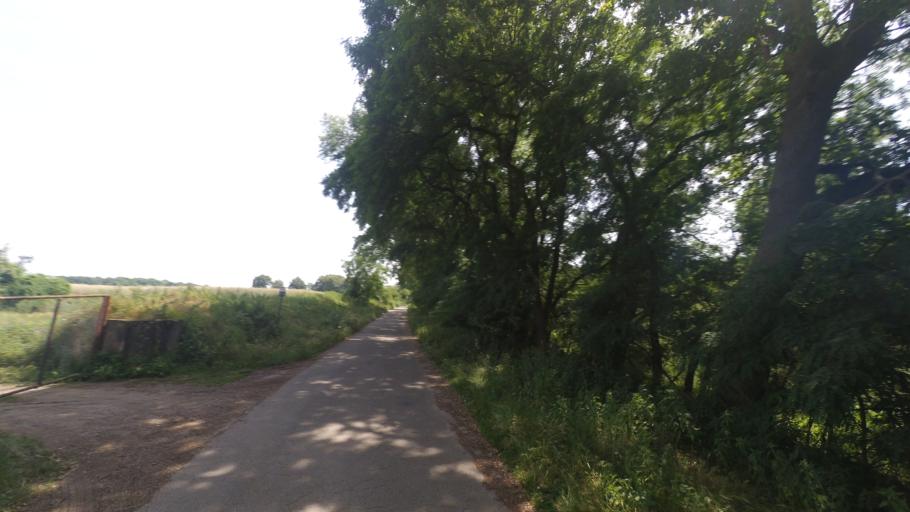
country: DE
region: Rheinland-Pfalz
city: Neuhofen
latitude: 49.4114
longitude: 8.4284
